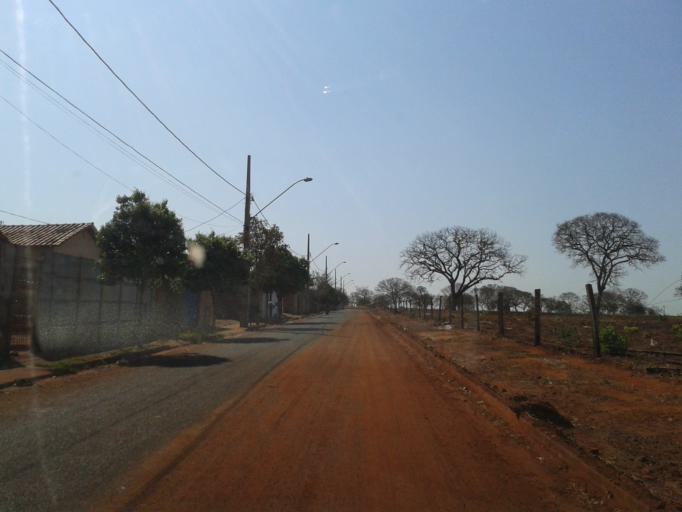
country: BR
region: Minas Gerais
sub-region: Ituiutaba
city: Ituiutaba
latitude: -18.9811
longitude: -49.4306
